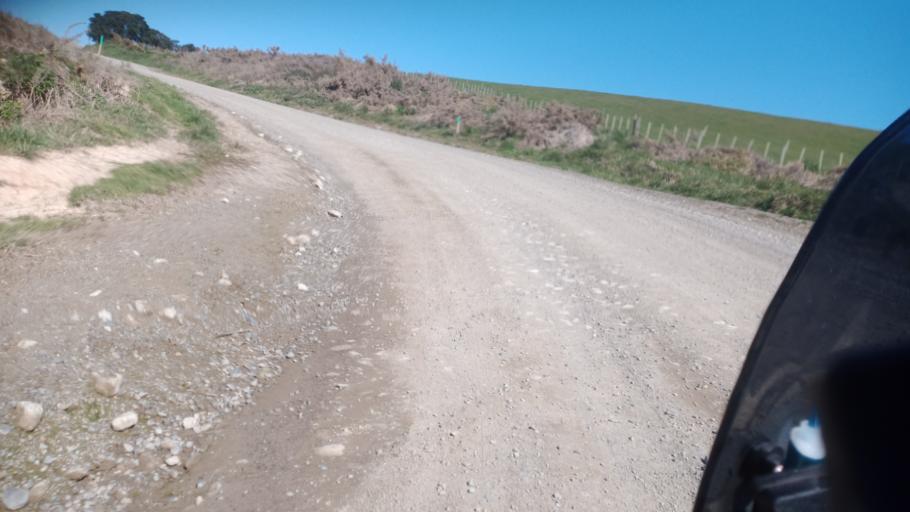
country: NZ
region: Gisborne
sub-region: Gisborne District
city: Gisborne
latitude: -39.1143
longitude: 177.9622
